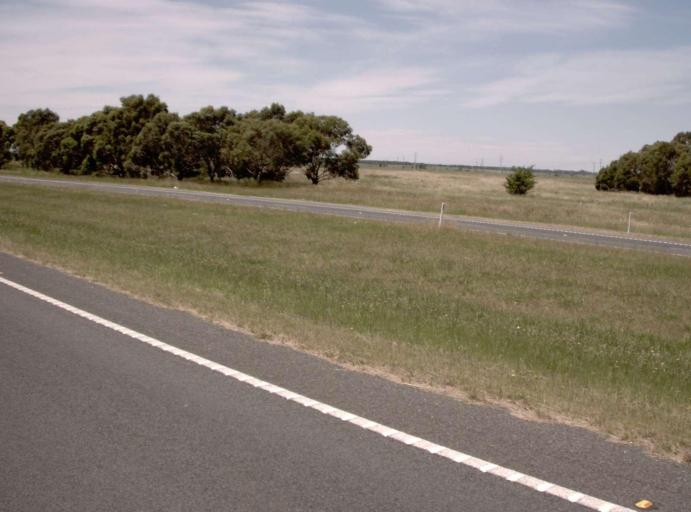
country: AU
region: Victoria
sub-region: Latrobe
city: Morwell
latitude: -38.2338
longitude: 146.4544
